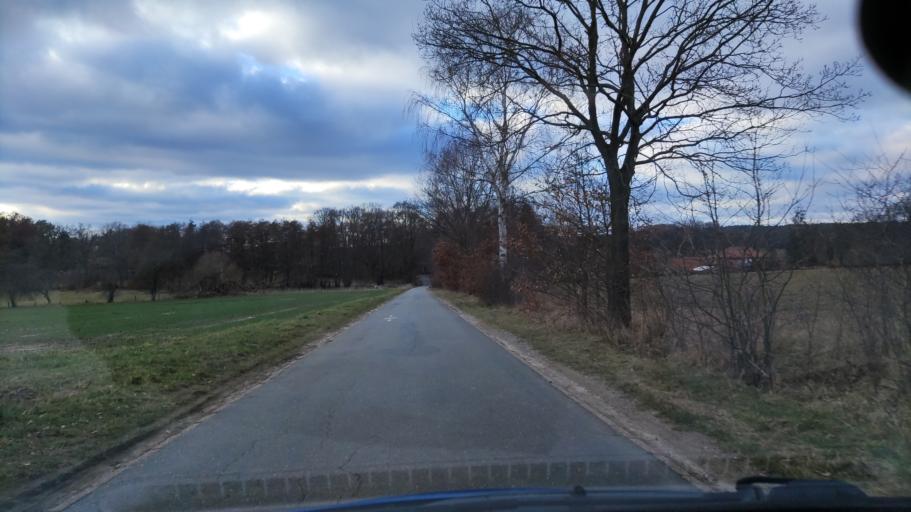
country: DE
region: Lower Saxony
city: Gohrde
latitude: 53.1616
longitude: 10.8711
